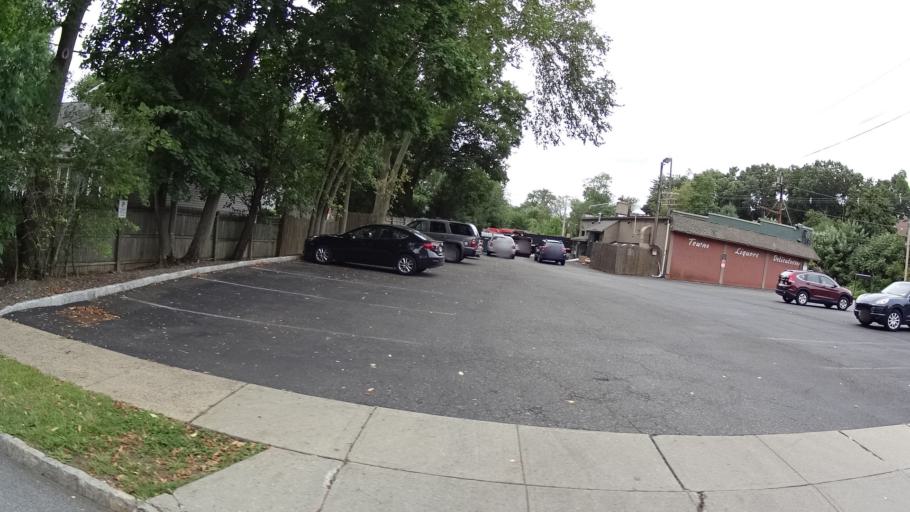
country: US
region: New Jersey
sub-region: Union County
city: New Providence
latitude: 40.7119
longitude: -74.3859
